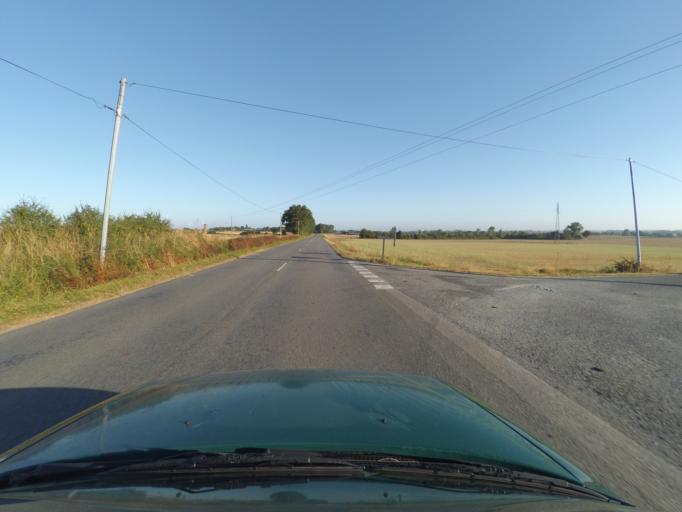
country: FR
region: Pays de la Loire
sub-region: Departement de la Loire-Atlantique
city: Vieillevigne
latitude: 46.9911
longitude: -1.4487
